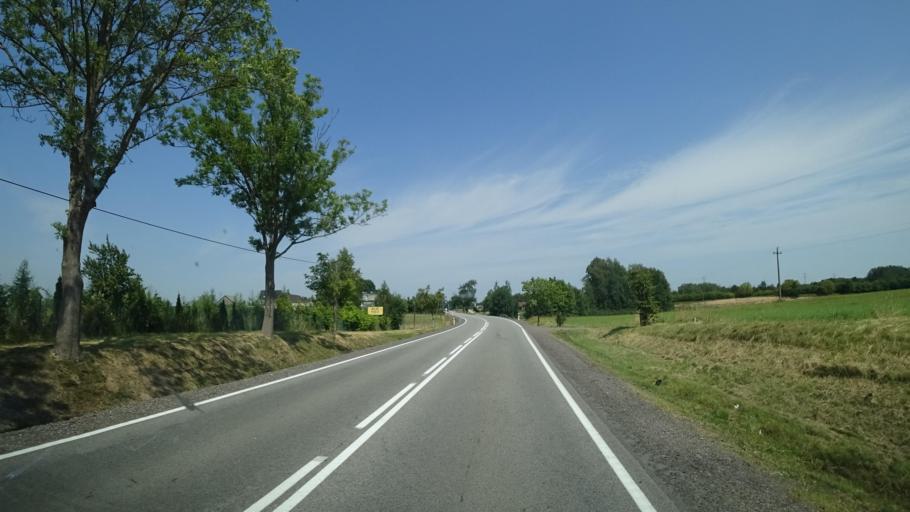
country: PL
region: Pomeranian Voivodeship
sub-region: Powiat koscierski
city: Koscierzyna
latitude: 54.1478
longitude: 18.0270
